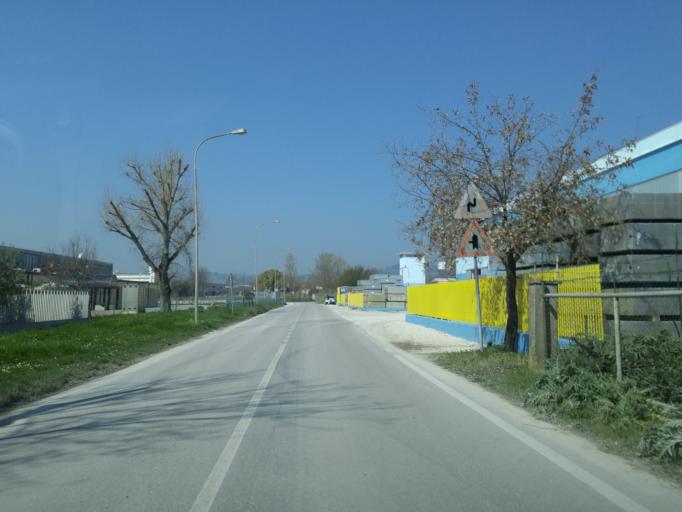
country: IT
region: The Marches
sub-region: Provincia di Pesaro e Urbino
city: Bellocchi
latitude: 43.7894
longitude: 13.0096
